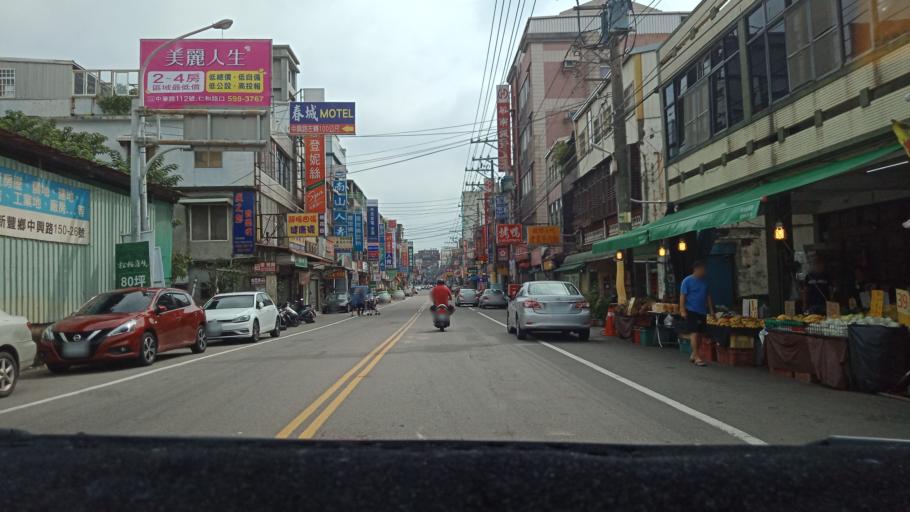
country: TW
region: Taiwan
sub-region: Hsinchu
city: Zhubei
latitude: 24.8753
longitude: 120.9944
